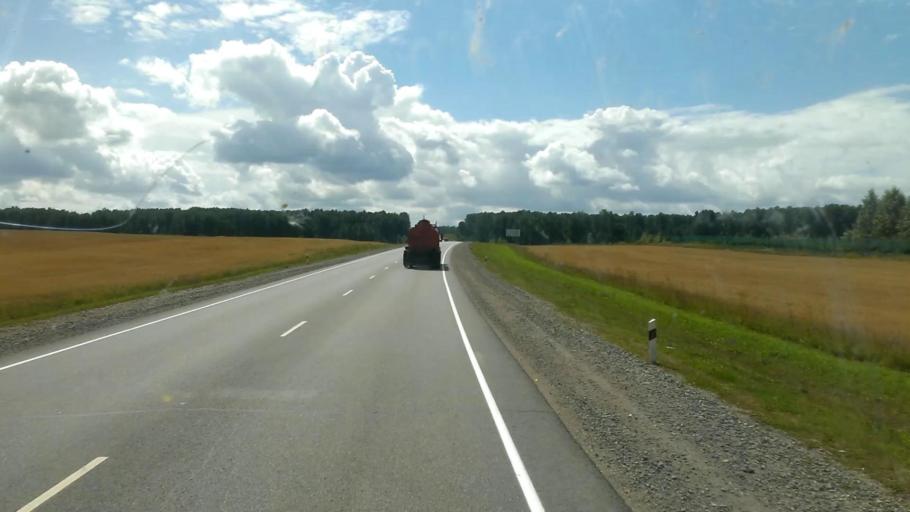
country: RU
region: Altai Krai
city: Troitskoye
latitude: 52.9877
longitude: 84.7433
